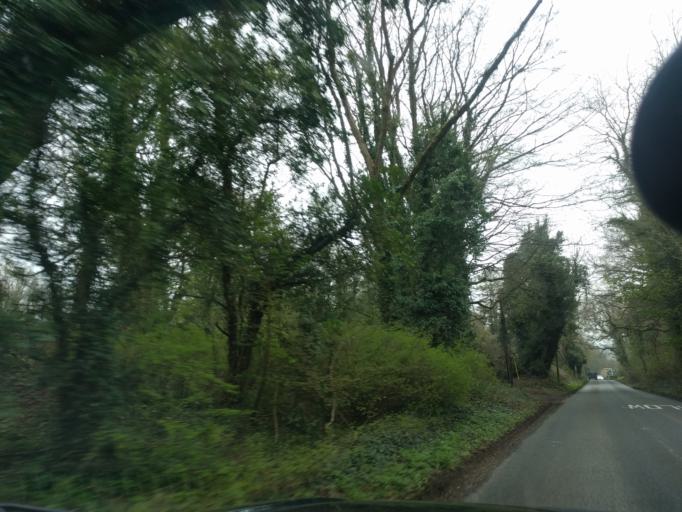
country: GB
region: England
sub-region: Wiltshire
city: Box
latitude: 51.4027
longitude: -2.2713
